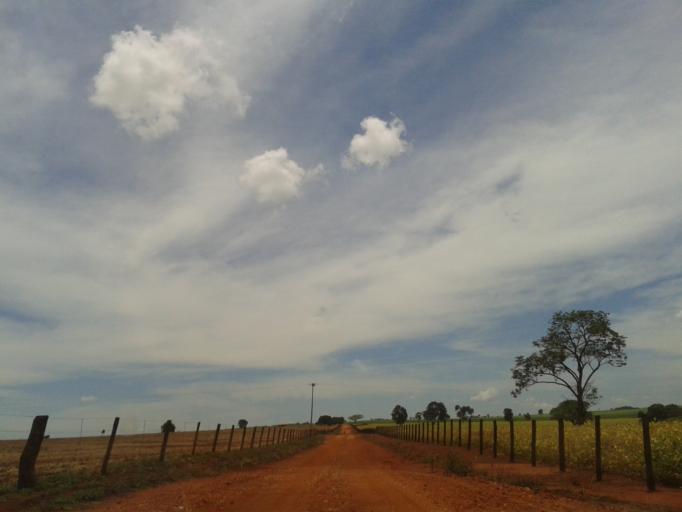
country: BR
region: Minas Gerais
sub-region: Capinopolis
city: Capinopolis
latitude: -18.7017
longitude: -49.7123
